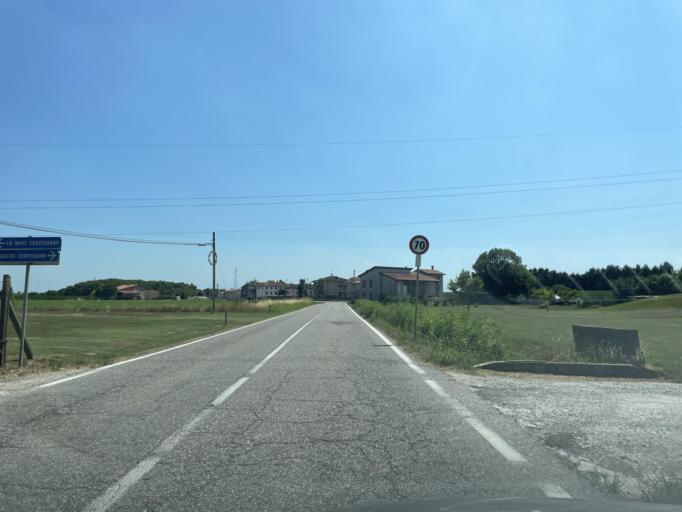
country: IT
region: Veneto
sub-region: Provincia di Verona
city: San Martino Buon Albergo
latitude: 45.3949
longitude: 11.0840
